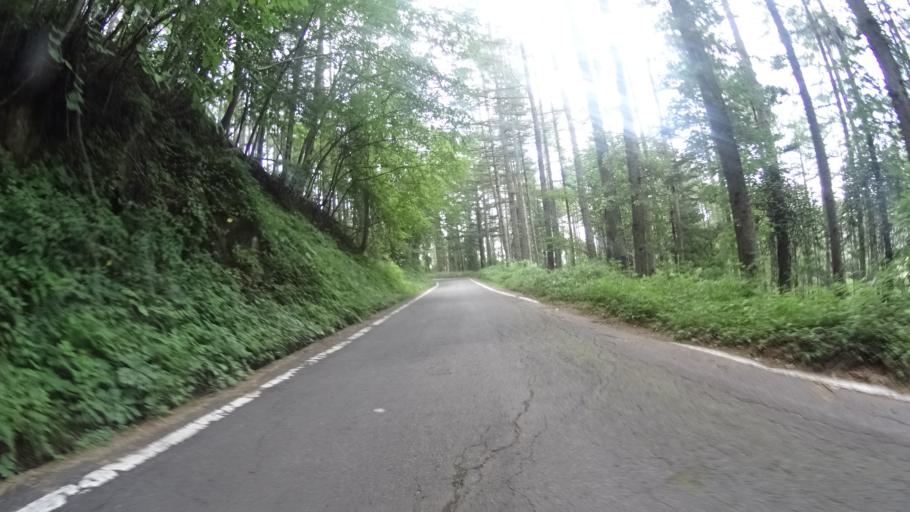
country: JP
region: Yamanashi
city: Enzan
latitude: 35.8377
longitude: 138.6401
